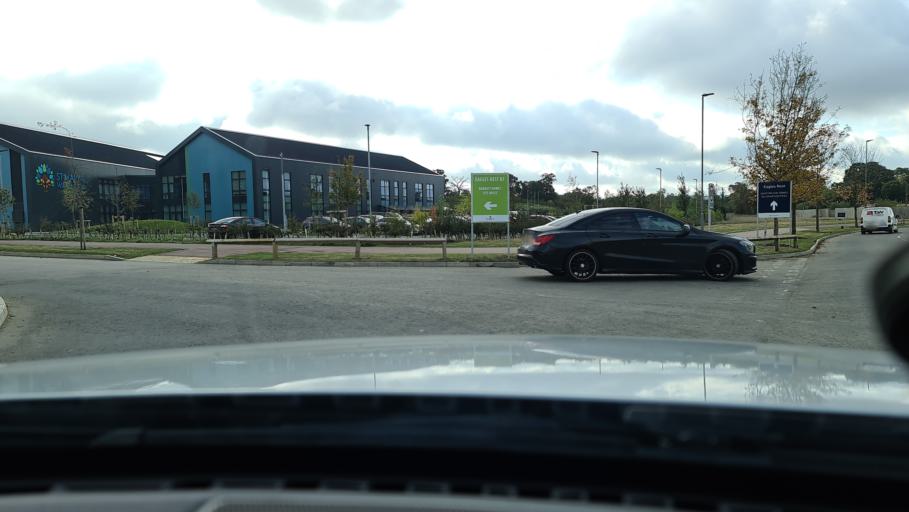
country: GB
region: England
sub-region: Milton Keynes
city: Woburn Sands
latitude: 52.0350
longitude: -0.6507
